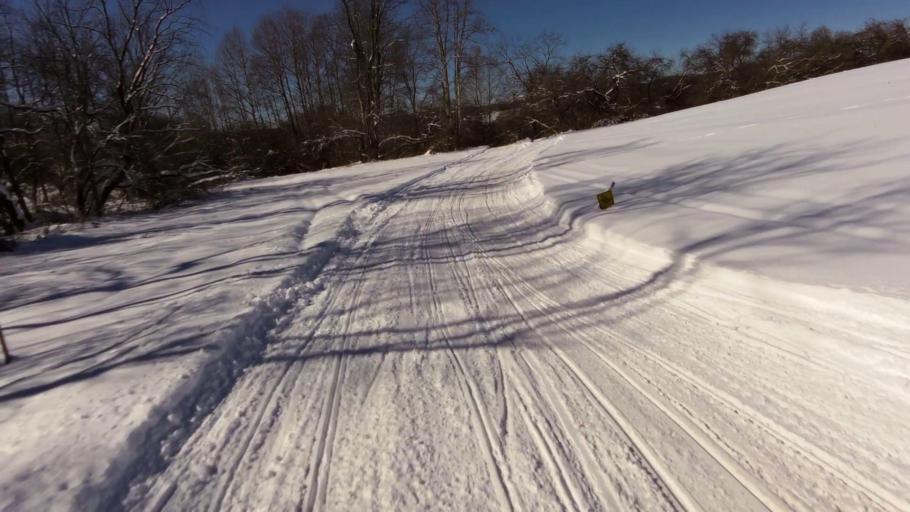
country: US
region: New York
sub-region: Chautauqua County
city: Mayville
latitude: 42.2476
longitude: -79.4269
